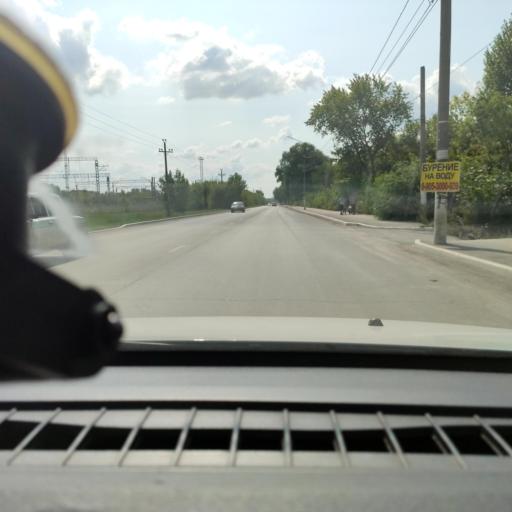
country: RU
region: Samara
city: Chapayevsk
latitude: 52.9831
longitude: 49.7073
